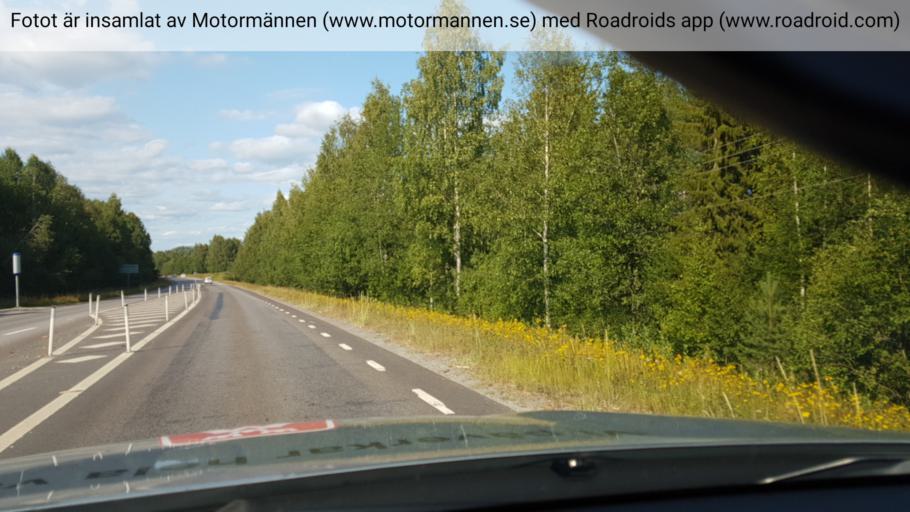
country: SE
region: Norrbotten
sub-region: Pitea Kommun
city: Pitea
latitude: 65.2987
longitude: 21.5105
